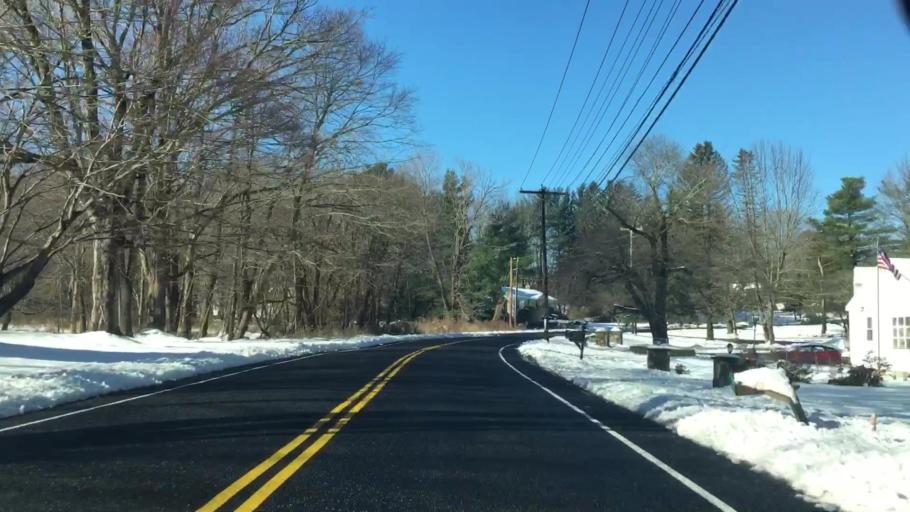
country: US
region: Connecticut
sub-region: Fairfield County
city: Shelton
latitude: 41.2977
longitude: -73.1544
